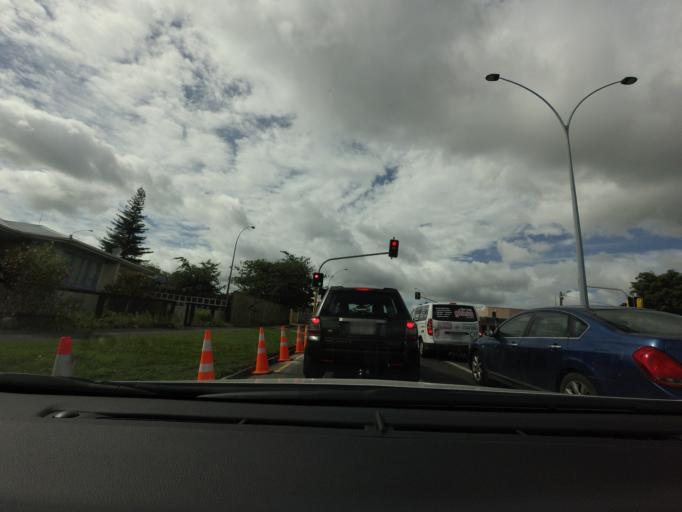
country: NZ
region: Bay of Plenty
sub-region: Rotorua District
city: Rotorua
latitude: -38.1443
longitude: 176.2377
